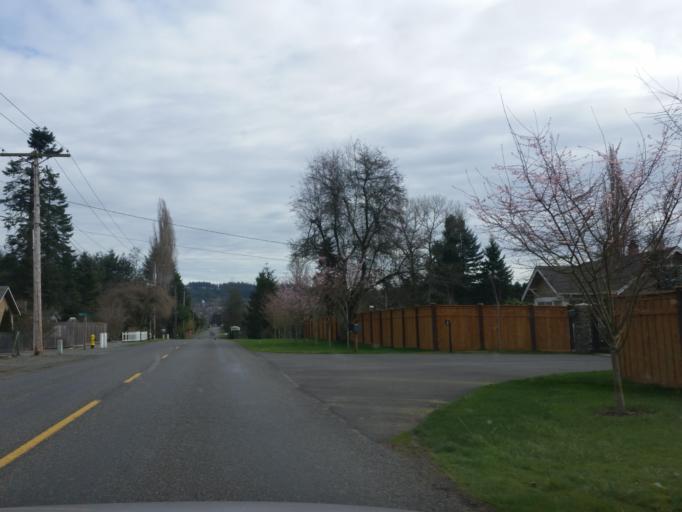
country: US
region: Washington
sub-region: Pierce County
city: Alderton
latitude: 47.1844
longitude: -122.2370
